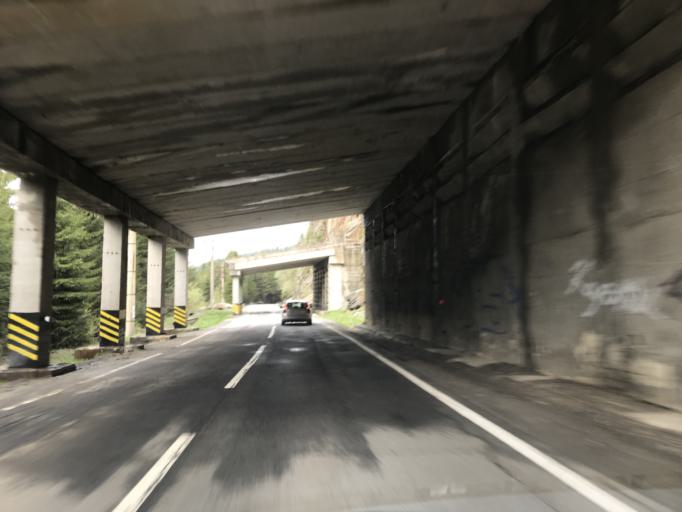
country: RO
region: Sibiu
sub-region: Comuna Cartisoara
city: Cartisoara
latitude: 45.6433
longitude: 24.6055
